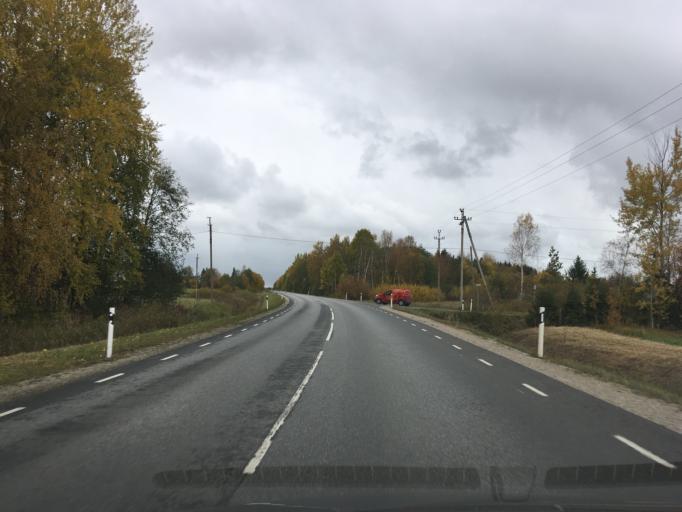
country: EE
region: Harju
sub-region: Anija vald
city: Kehra
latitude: 59.3206
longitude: 25.3417
